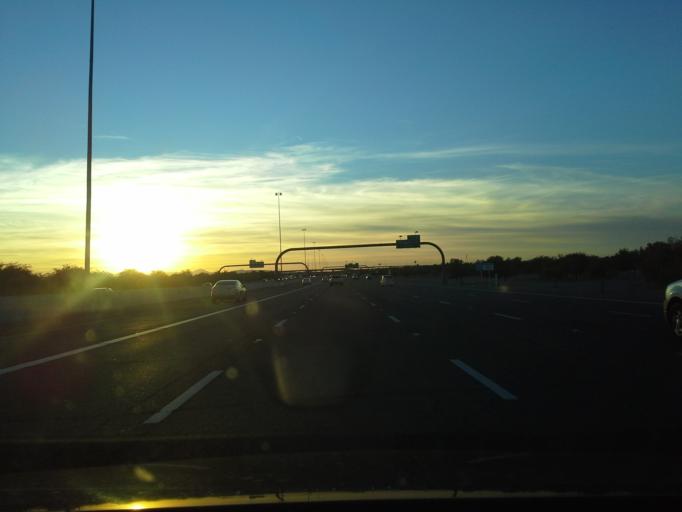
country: US
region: Arizona
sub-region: Pinal County
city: Apache Junction
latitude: 33.3867
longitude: -111.6216
